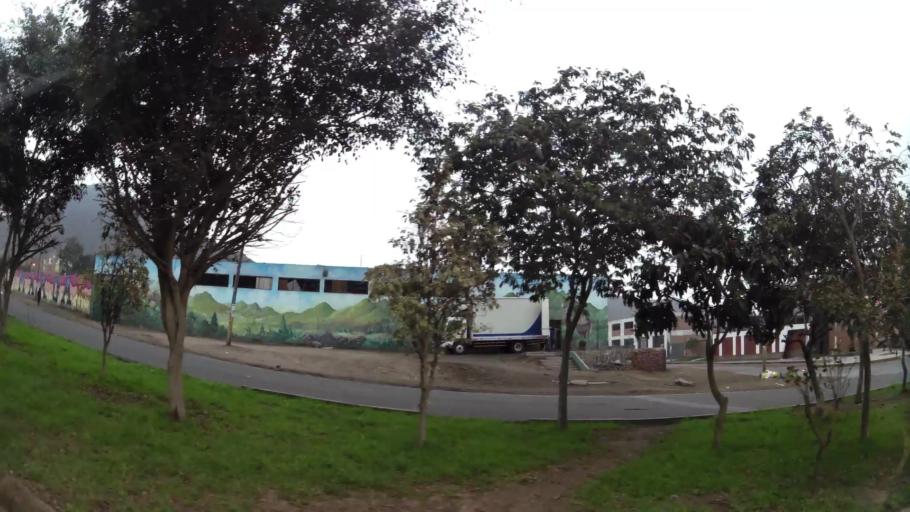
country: PE
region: Lima
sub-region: Lima
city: Vitarte
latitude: -12.0105
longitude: -76.9811
